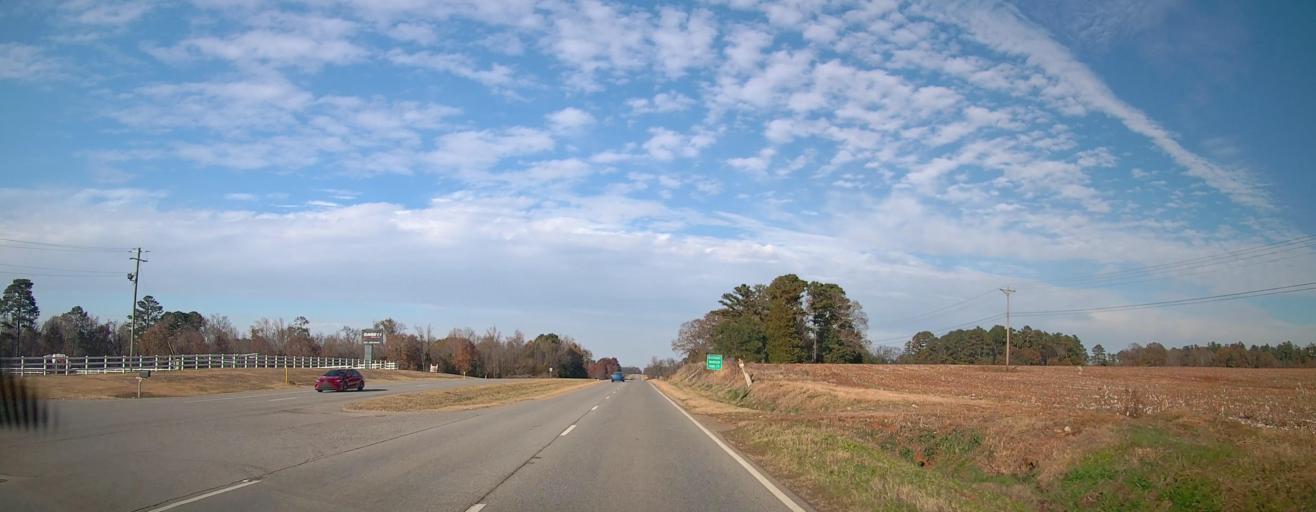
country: US
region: Alabama
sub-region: Morgan County
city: Decatur
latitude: 34.6697
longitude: -86.9499
